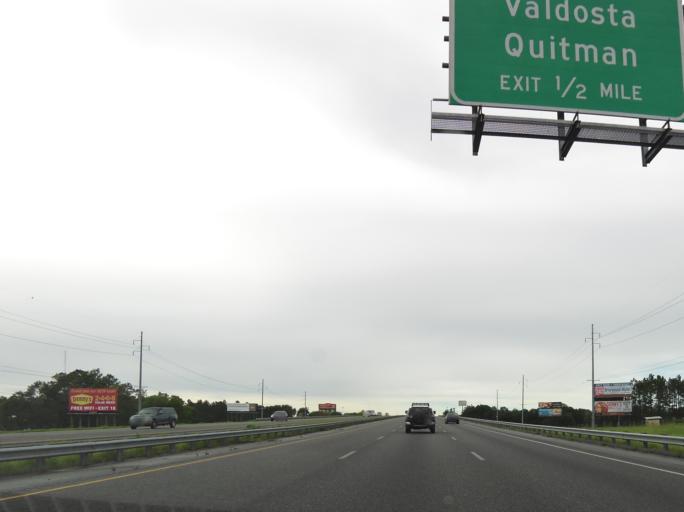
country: US
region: Georgia
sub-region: Lowndes County
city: Remerton
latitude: 30.8124
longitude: -83.3132
